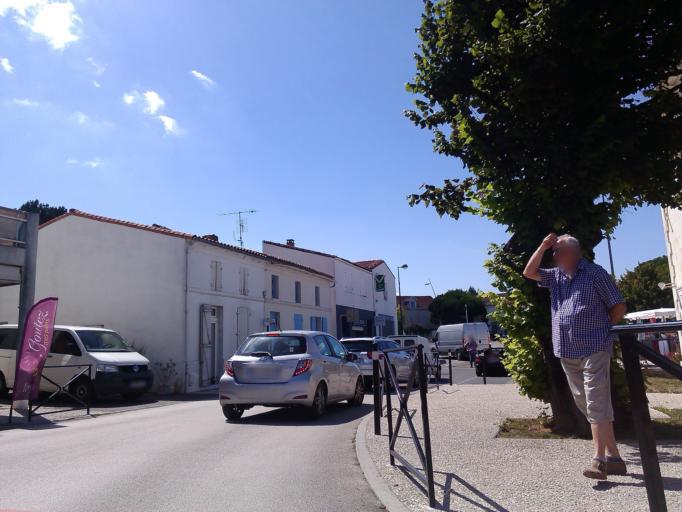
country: FR
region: Poitou-Charentes
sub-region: Departement de la Charente-Maritime
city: Vaux-sur-Mer
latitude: 45.6451
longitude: -1.0603
